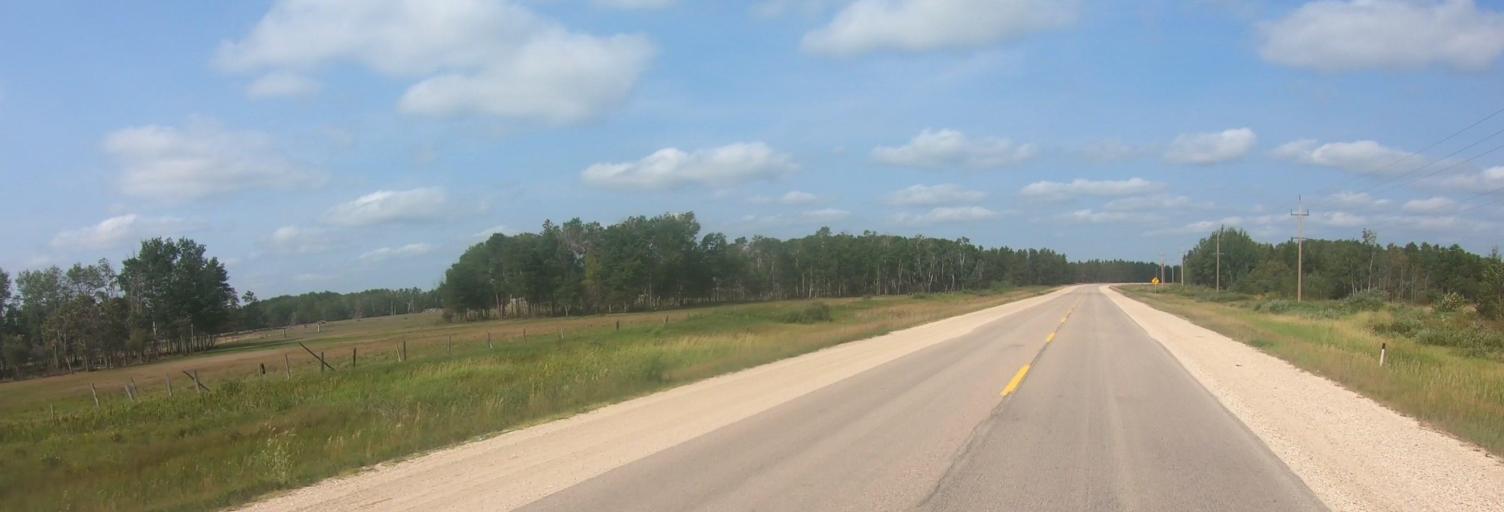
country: CA
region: Manitoba
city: La Broquerie
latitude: 49.2352
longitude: -96.3404
